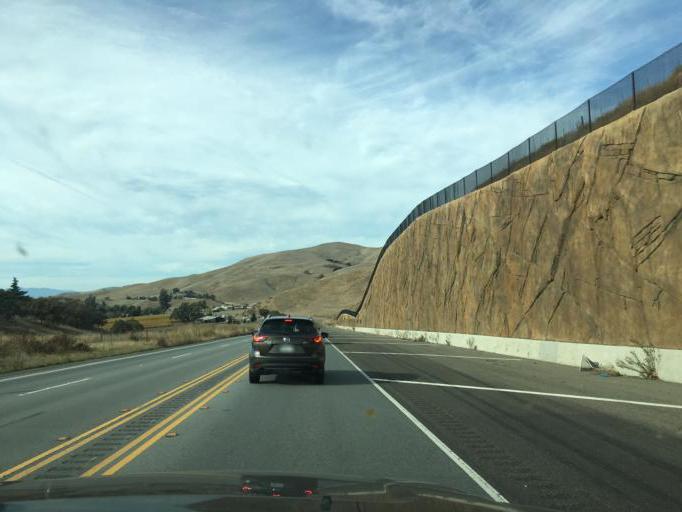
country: US
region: California
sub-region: San Benito County
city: Hollister
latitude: 36.9660
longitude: -121.4102
